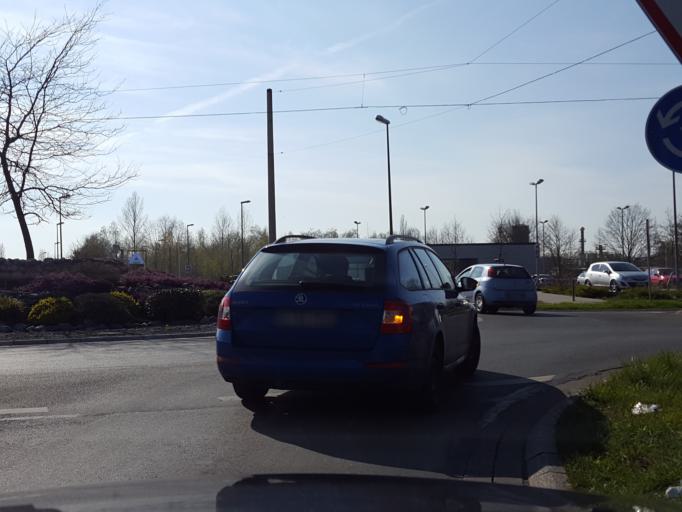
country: DE
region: North Rhine-Westphalia
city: Castrop-Rauxel
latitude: 51.5796
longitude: 7.3047
